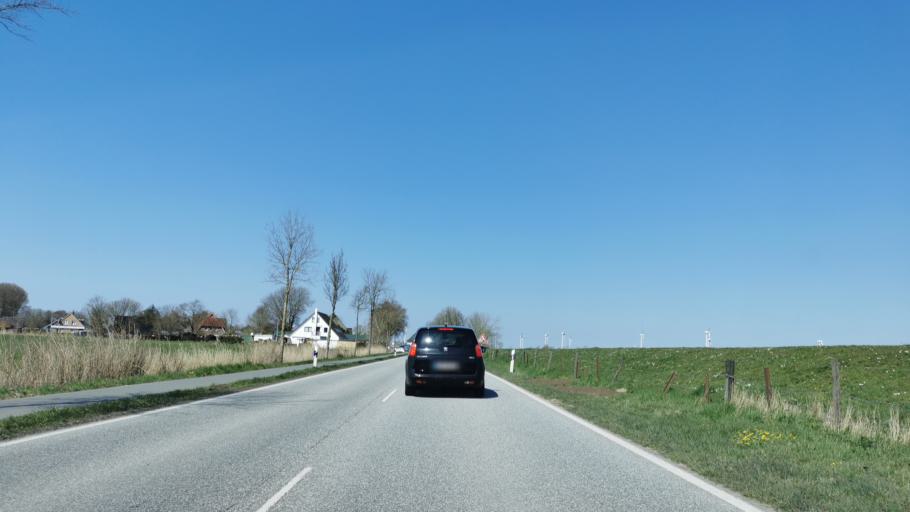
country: DE
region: Schleswig-Holstein
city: Wesselburener Deichhausen
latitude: 54.1563
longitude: 8.9102
